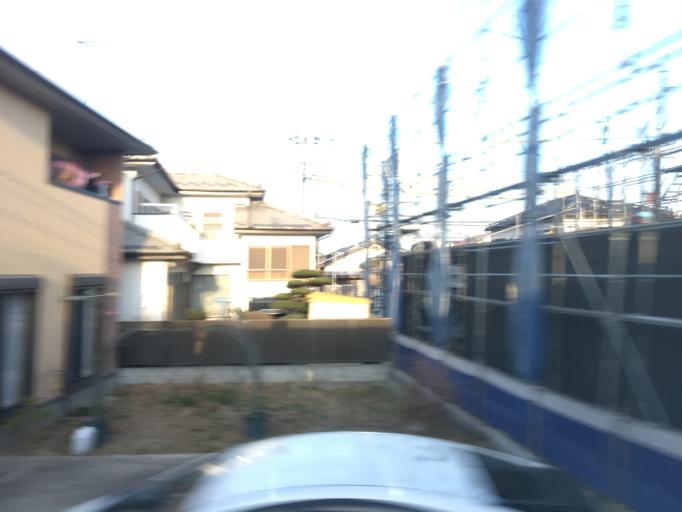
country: JP
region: Saitama
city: Konosu
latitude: 36.0647
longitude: 139.5058
